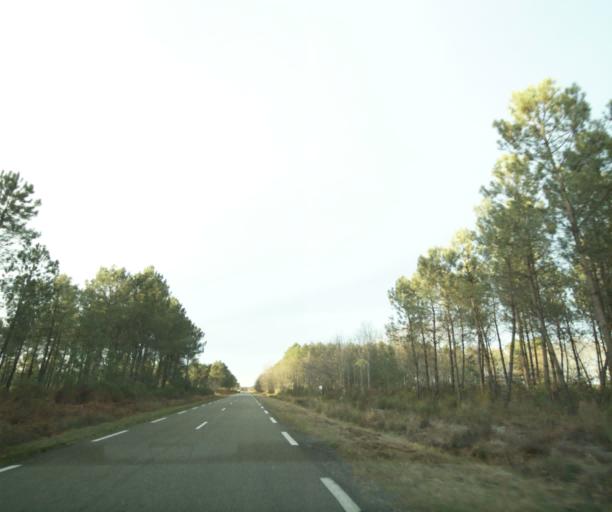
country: FR
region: Aquitaine
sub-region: Departement des Landes
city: Gabarret
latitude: 44.1440
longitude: -0.1231
